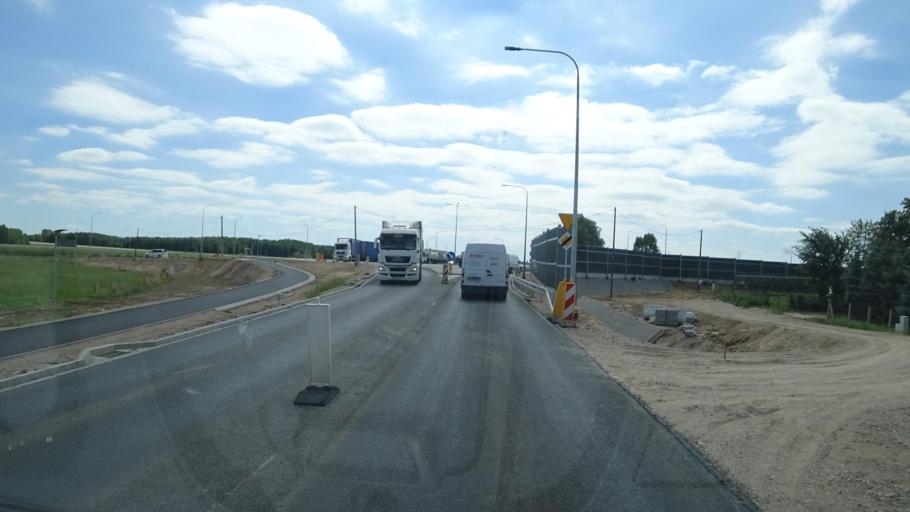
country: PL
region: Warmian-Masurian Voivodeship
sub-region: Powiat elcki
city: Elk
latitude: 53.7599
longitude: 22.3382
